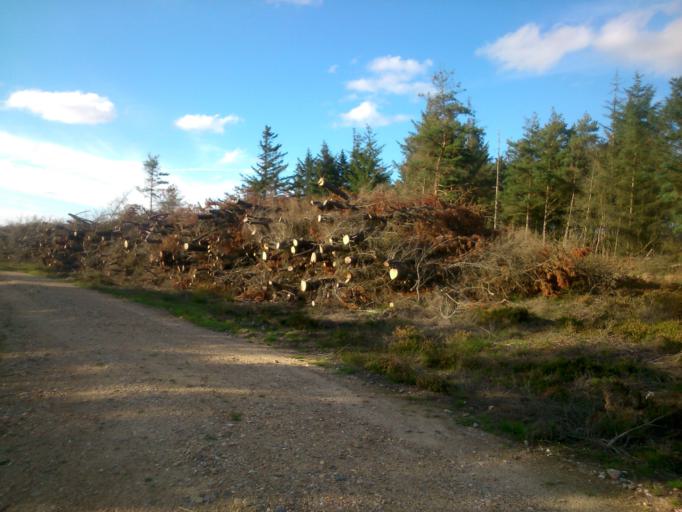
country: DK
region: South Denmark
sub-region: Varde Kommune
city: Oksbol
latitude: 55.6996
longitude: 8.1778
